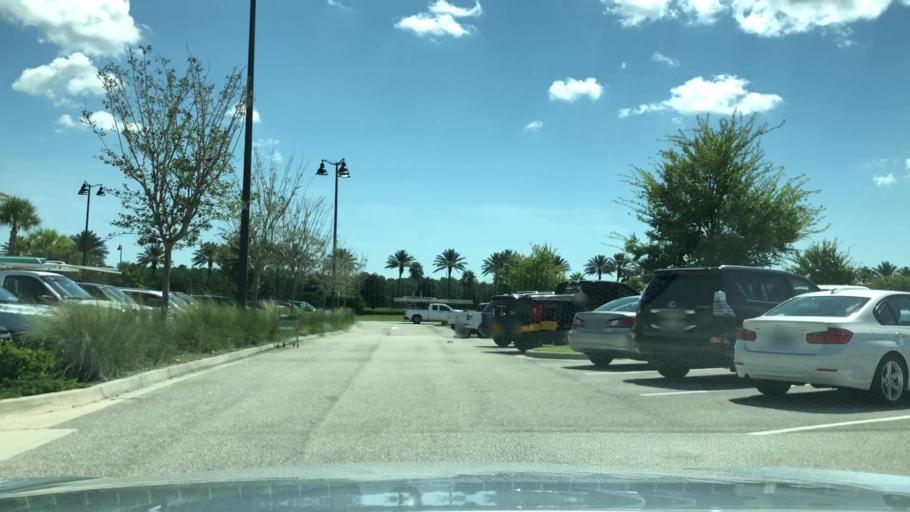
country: US
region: Florida
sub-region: Saint Johns County
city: Palm Valley
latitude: 30.1113
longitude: -81.4191
